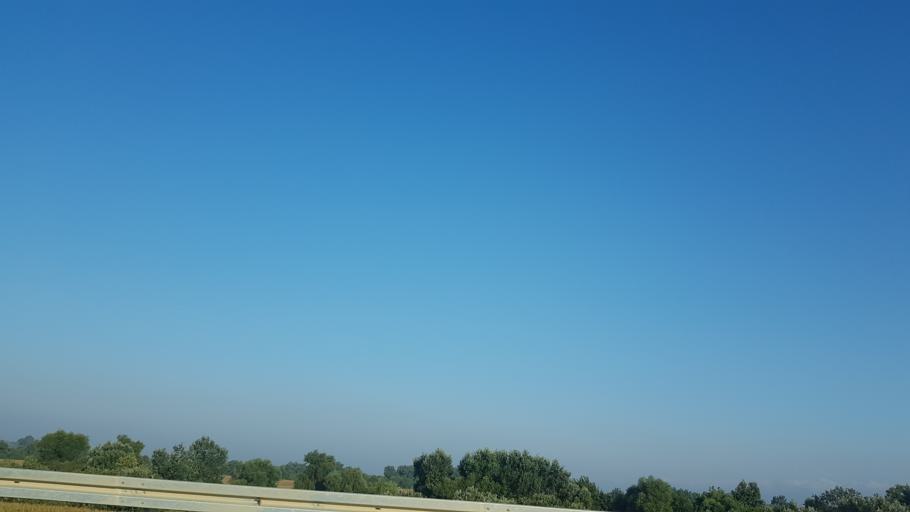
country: TR
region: Bursa
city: Karacabey
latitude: 40.1795
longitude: 28.3286
